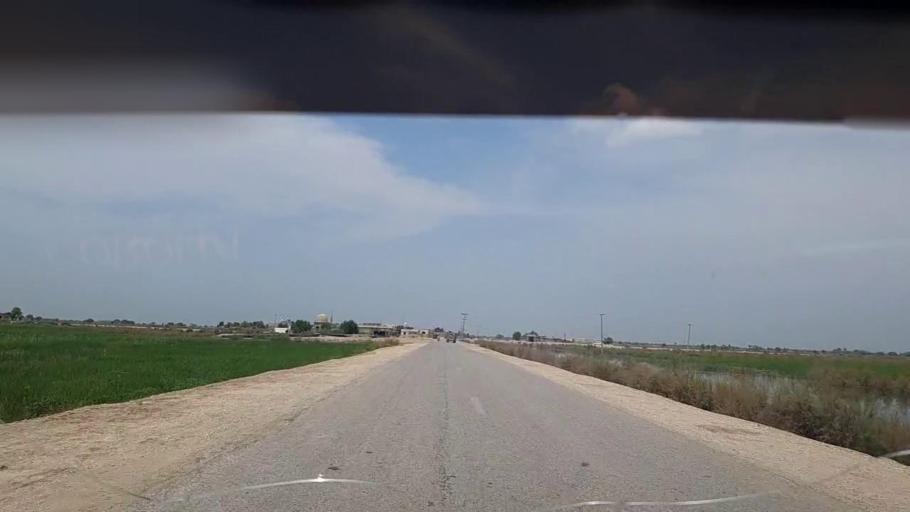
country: PK
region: Sindh
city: Thul
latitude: 28.1970
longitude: 68.7917
